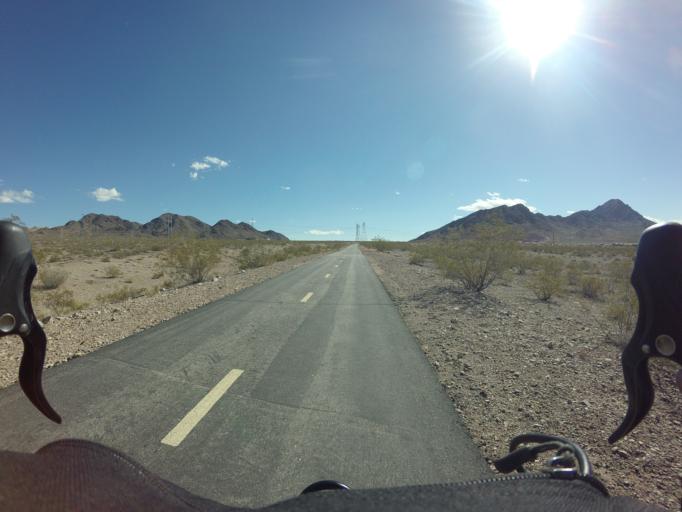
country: US
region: Nevada
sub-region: Clark County
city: Henderson
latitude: 35.9915
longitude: -114.9210
